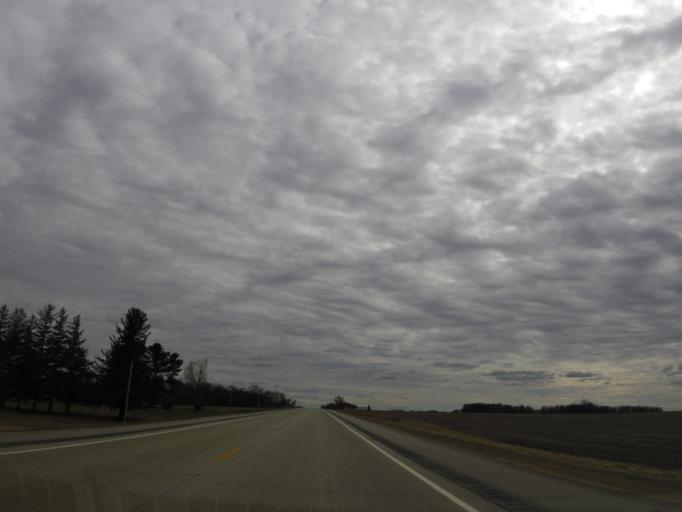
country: US
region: Minnesota
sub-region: Fillmore County
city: Spring Valley
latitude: 43.5216
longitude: -92.3694
